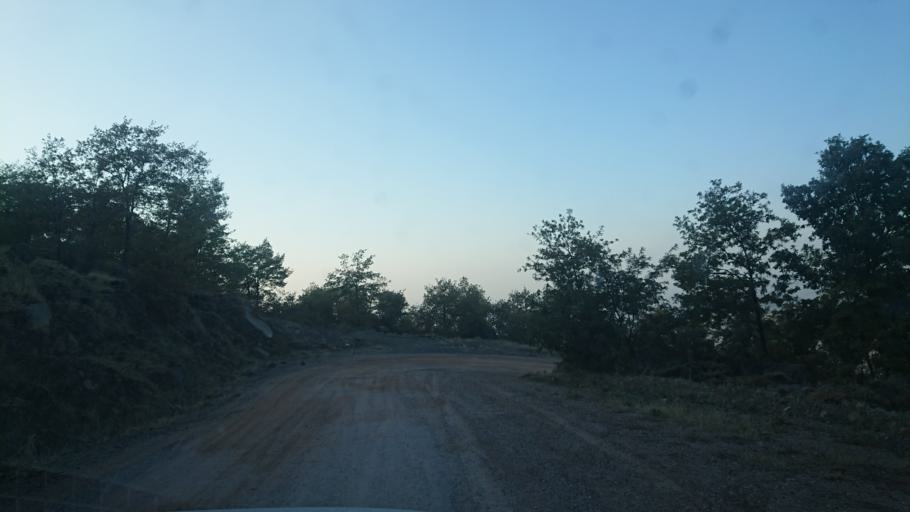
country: TR
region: Aksaray
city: Taspinar
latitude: 38.1707
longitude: 34.1795
